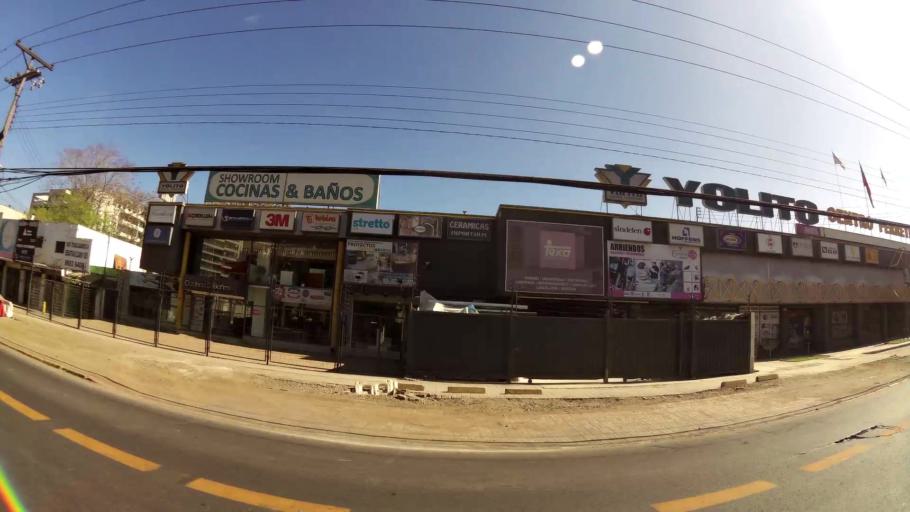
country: CL
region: Santiago Metropolitan
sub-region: Provincia de Santiago
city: Villa Presidente Frei, Nunoa, Santiago, Chile
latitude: -33.4050
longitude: -70.5580
